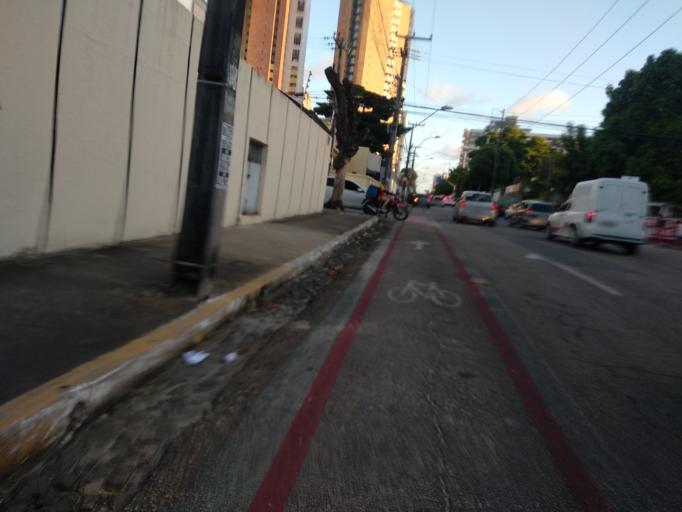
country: BR
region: Ceara
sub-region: Fortaleza
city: Fortaleza
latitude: -3.7391
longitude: -38.5104
